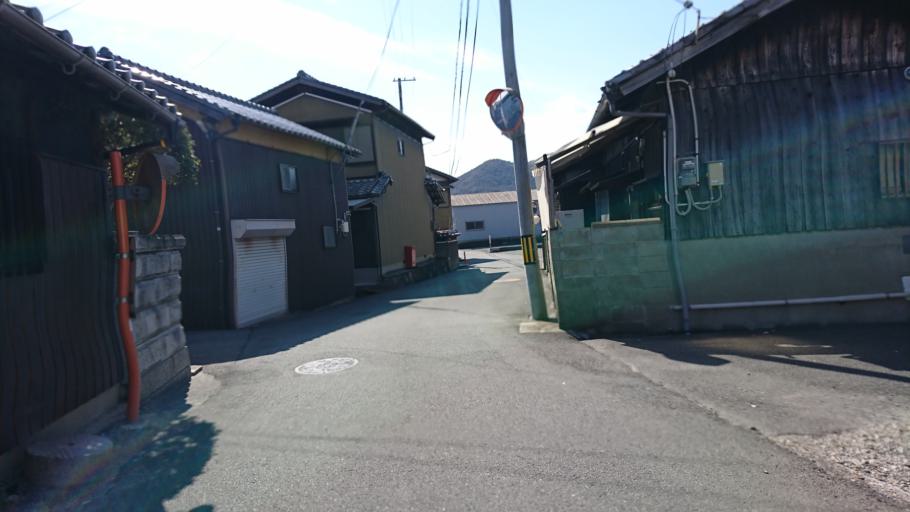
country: JP
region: Hyogo
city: Kakogawacho-honmachi
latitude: 34.8087
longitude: 134.8120
